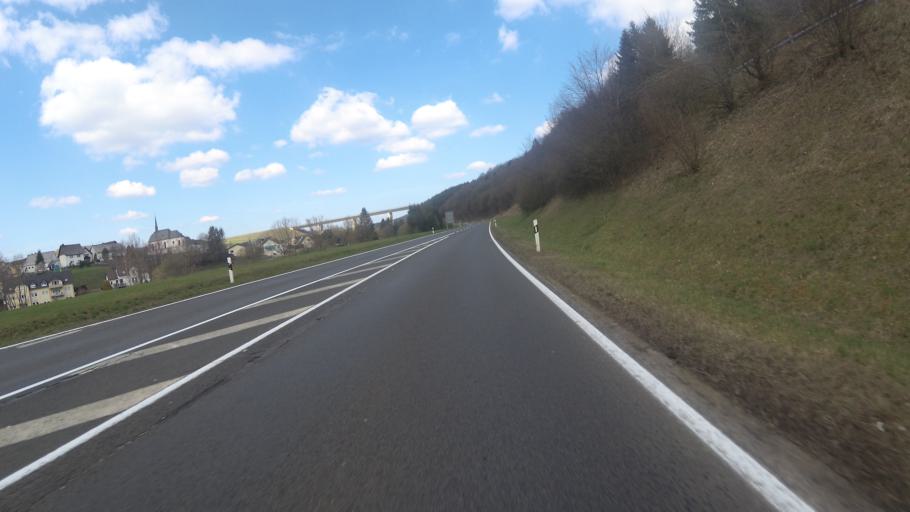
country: DE
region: Rheinland-Pfalz
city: Horscheid
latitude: 50.2210
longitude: 6.8452
